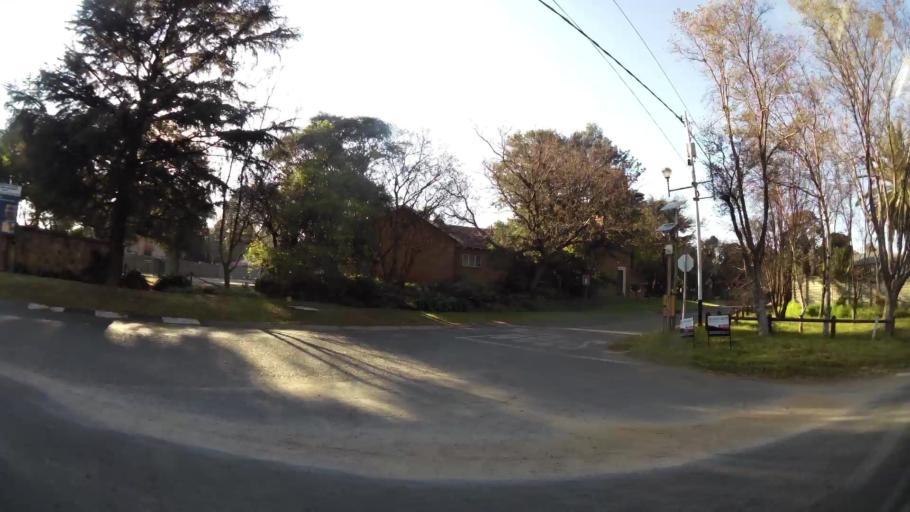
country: ZA
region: Gauteng
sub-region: City of Johannesburg Metropolitan Municipality
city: Johannesburg
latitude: -26.1189
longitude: 28.0756
